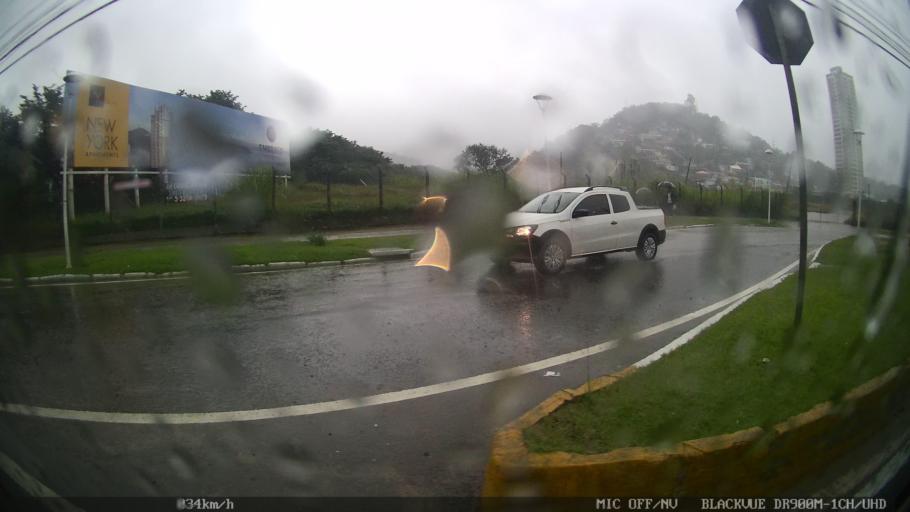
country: BR
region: Santa Catarina
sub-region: Balneario Camboriu
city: Balneario Camboriu
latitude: -26.9513
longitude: -48.6407
